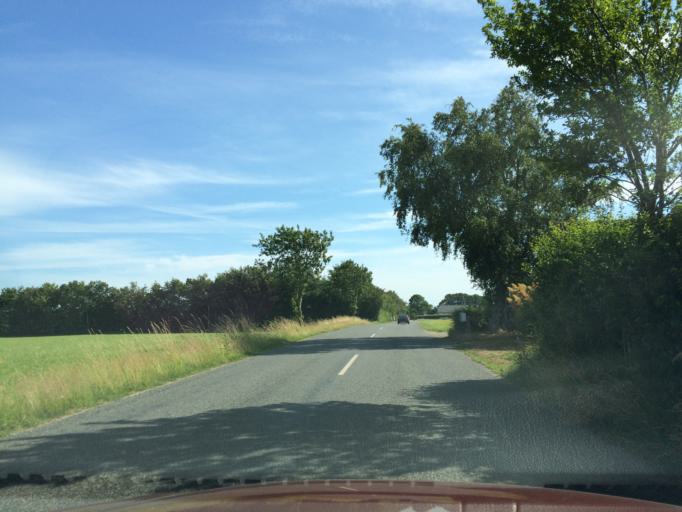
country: DK
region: Central Jutland
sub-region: Silkeborg Kommune
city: Svejbaek
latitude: 56.2281
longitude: 9.6656
